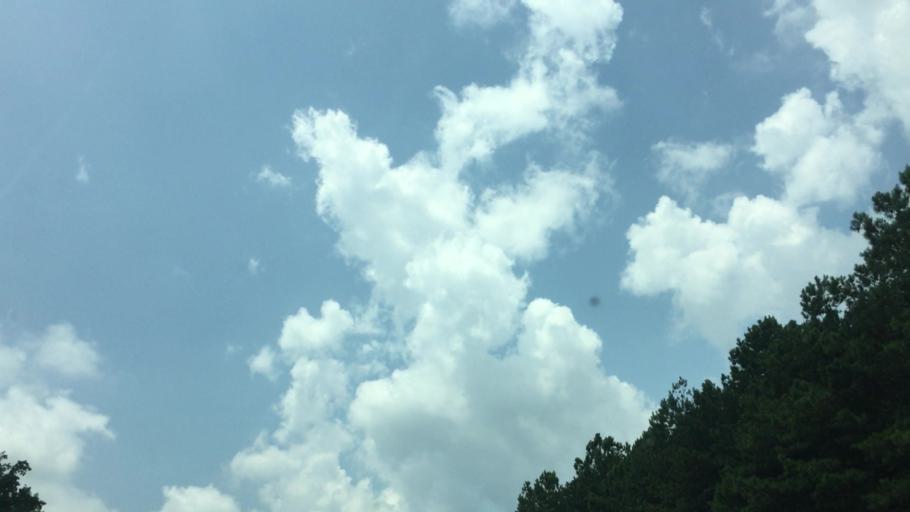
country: US
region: Georgia
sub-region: Carroll County
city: Villa Rica
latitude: 33.6151
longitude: -84.9377
